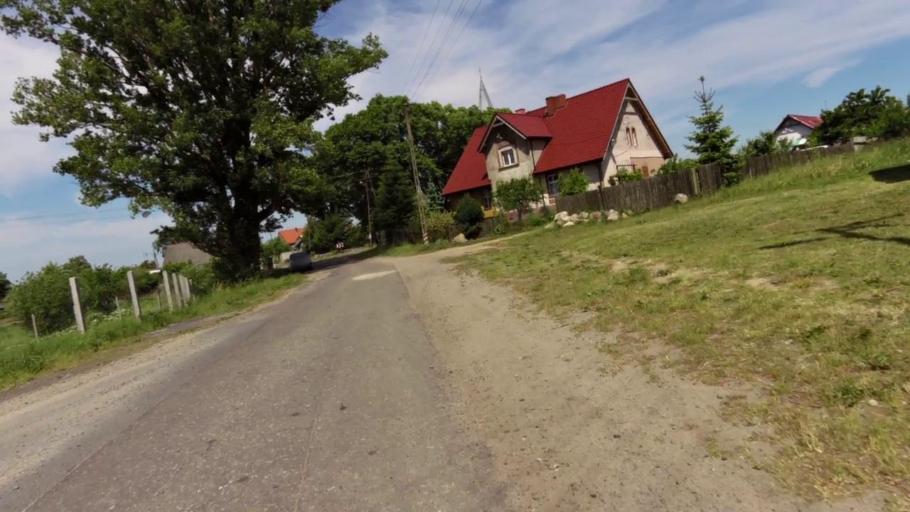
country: PL
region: West Pomeranian Voivodeship
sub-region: Powiat szczecinecki
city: Szczecinek
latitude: 53.6575
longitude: 16.6685
